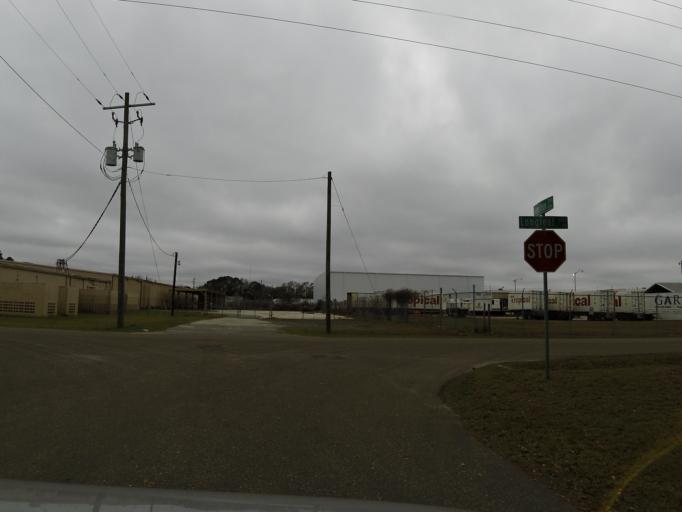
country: US
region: Florida
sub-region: Duval County
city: Jacksonville
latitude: 30.3657
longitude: -81.7120
